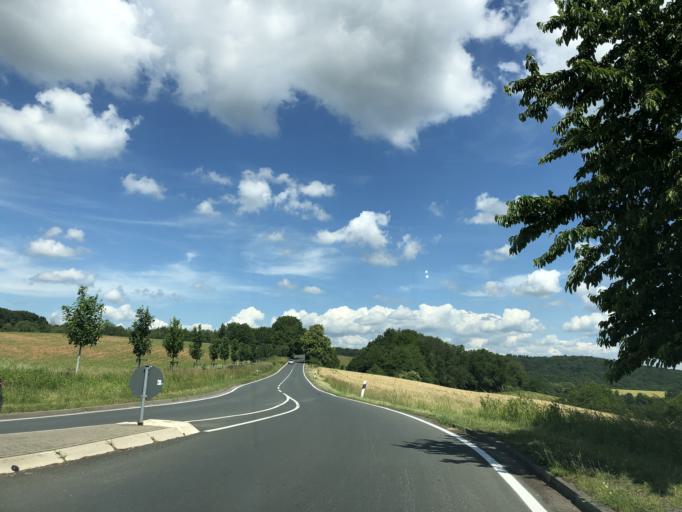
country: DE
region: Hesse
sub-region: Regierungsbezirk Giessen
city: Marburg an der Lahn
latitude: 50.8122
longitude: 8.7311
